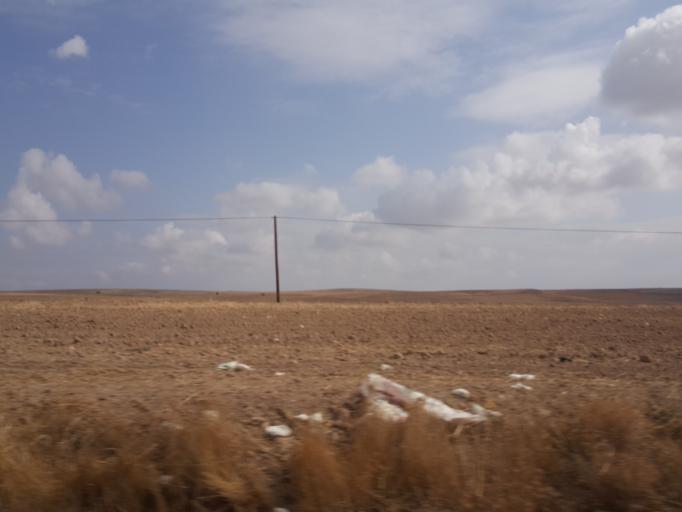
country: TR
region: Kirikkale
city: Keskin
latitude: 39.6115
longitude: 33.6132
